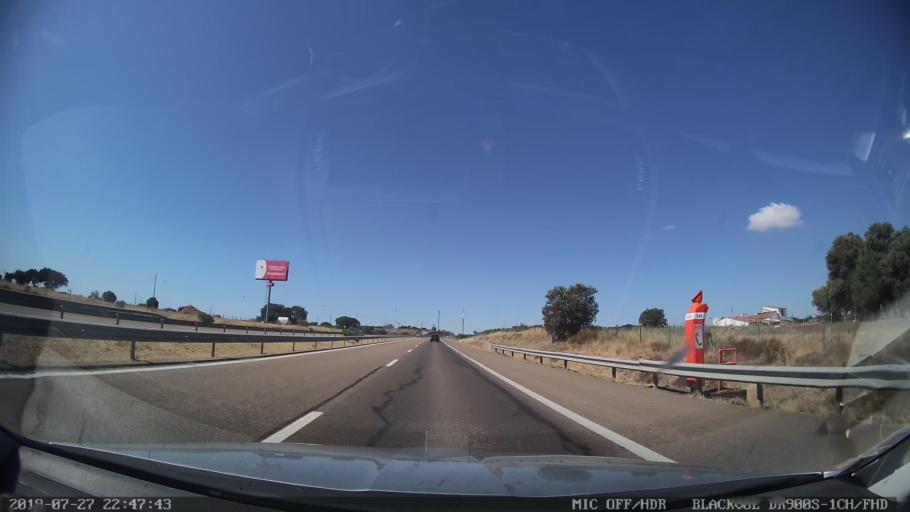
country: PT
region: Portalegre
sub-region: Elvas
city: Elvas
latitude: 38.8908
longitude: -7.2131
